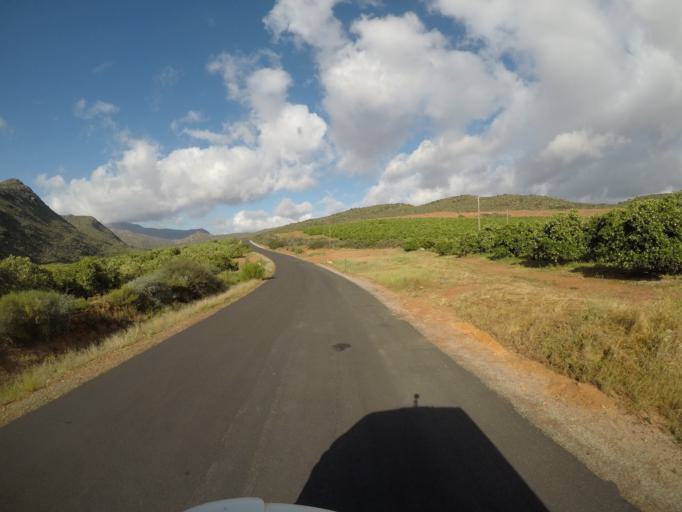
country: ZA
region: Western Cape
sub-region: West Coast District Municipality
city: Clanwilliam
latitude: -32.4317
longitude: 18.9492
